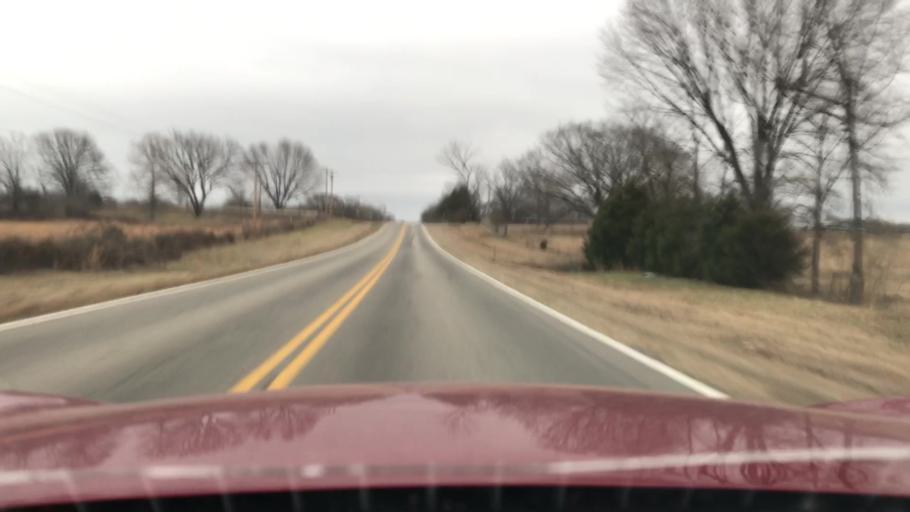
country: US
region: Oklahoma
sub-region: Sequoyah County
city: Sallisaw
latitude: 35.5070
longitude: -94.7632
